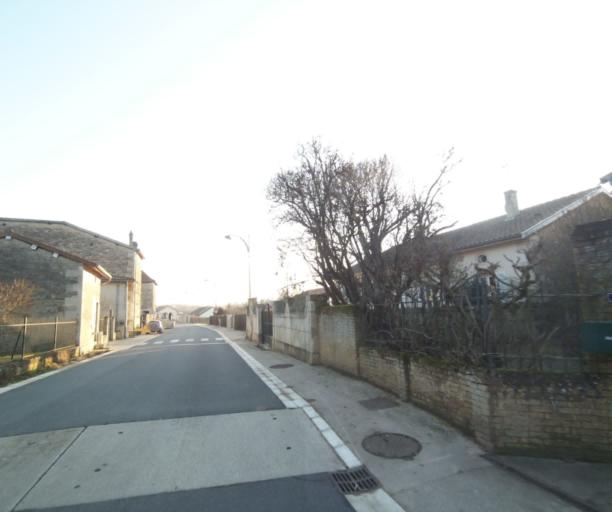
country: FR
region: Champagne-Ardenne
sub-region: Departement de la Haute-Marne
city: Chevillon
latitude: 48.5433
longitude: 5.1019
